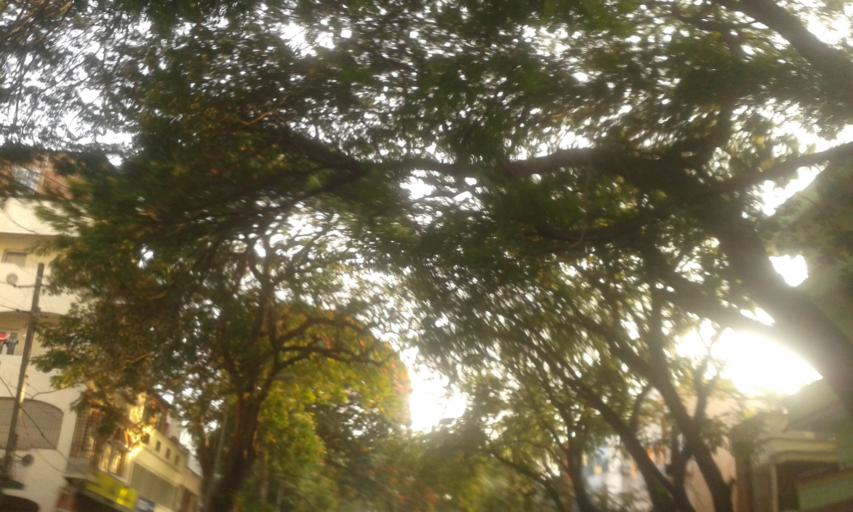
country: IN
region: Karnataka
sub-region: Bangalore Urban
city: Bangalore
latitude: 12.9182
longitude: 77.5951
